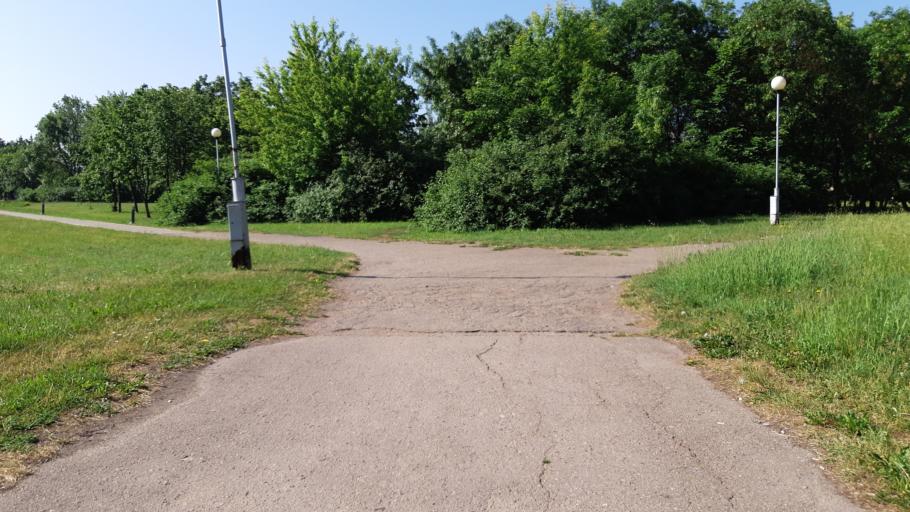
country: LT
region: Kauno apskritis
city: Dainava (Kaunas)
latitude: 54.9227
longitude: 23.9814
